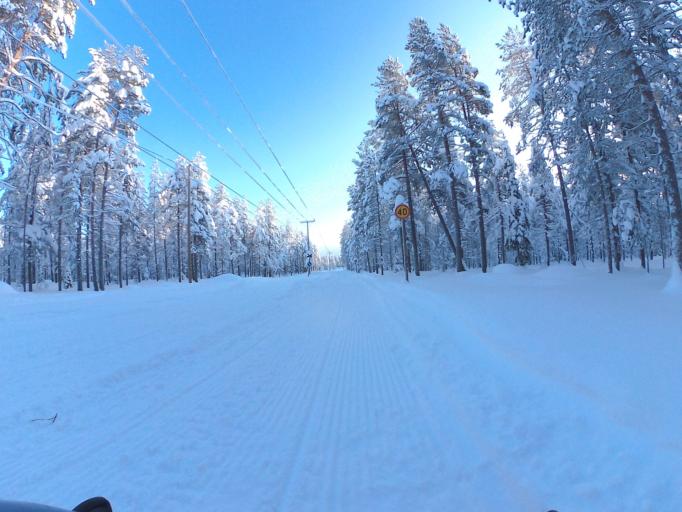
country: FI
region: Lapland
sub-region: Rovaniemi
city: Rovaniemi
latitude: 66.5482
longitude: 25.8577
